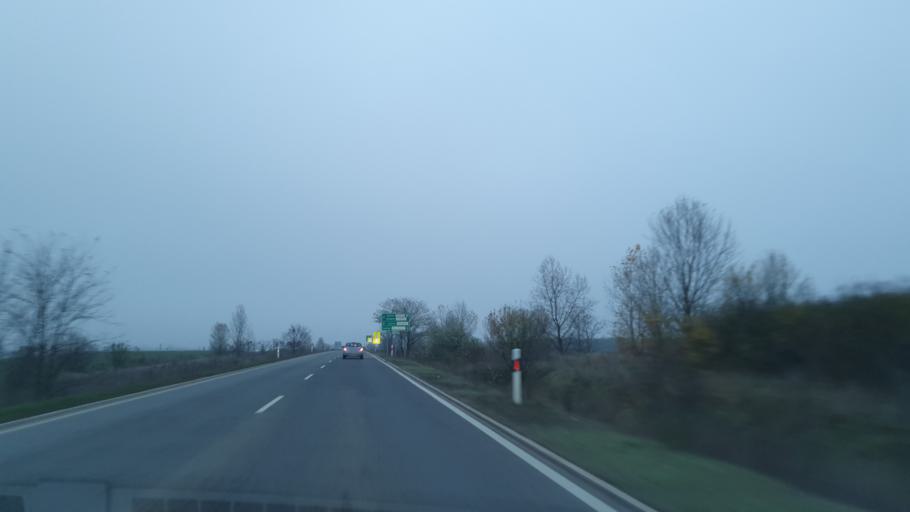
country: HU
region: Pest
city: Csomor
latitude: 47.5485
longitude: 19.1971
